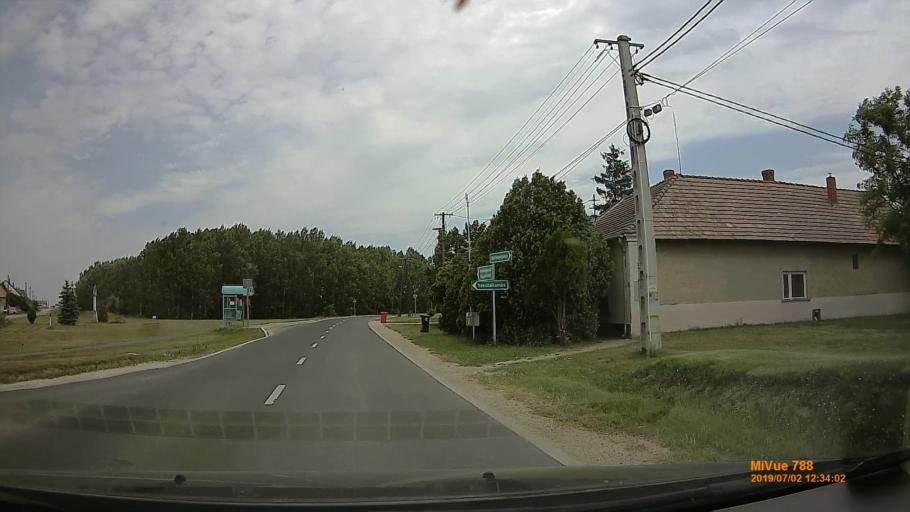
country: HU
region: Gyor-Moson-Sopron
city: Janossomorja
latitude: 47.8513
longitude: 17.1647
